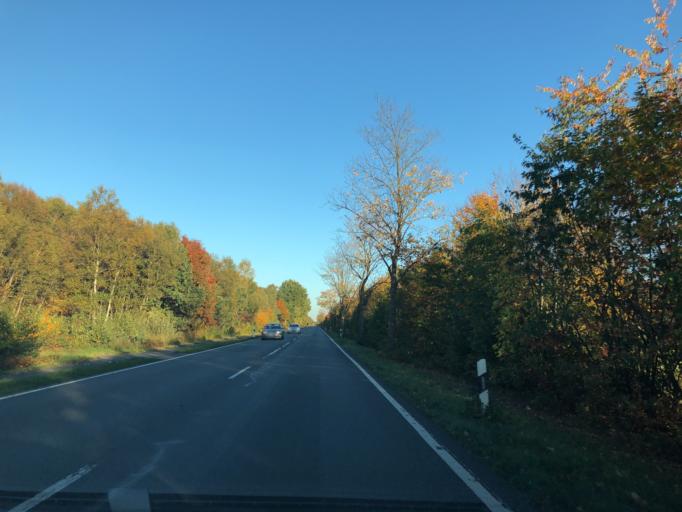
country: DE
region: Lower Saxony
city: Esterwegen
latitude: 53.0175
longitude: 7.6541
